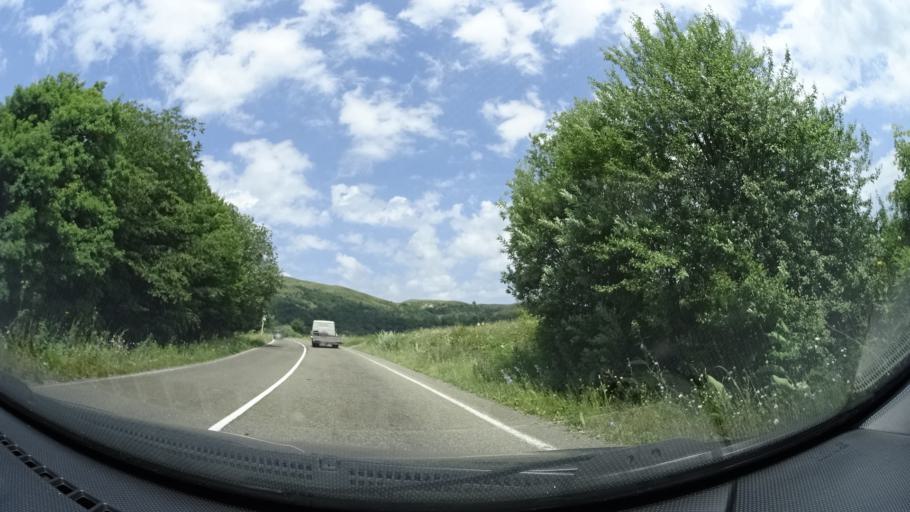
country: GE
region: Kakheti
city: Sagarejo
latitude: 41.8636
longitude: 45.2959
